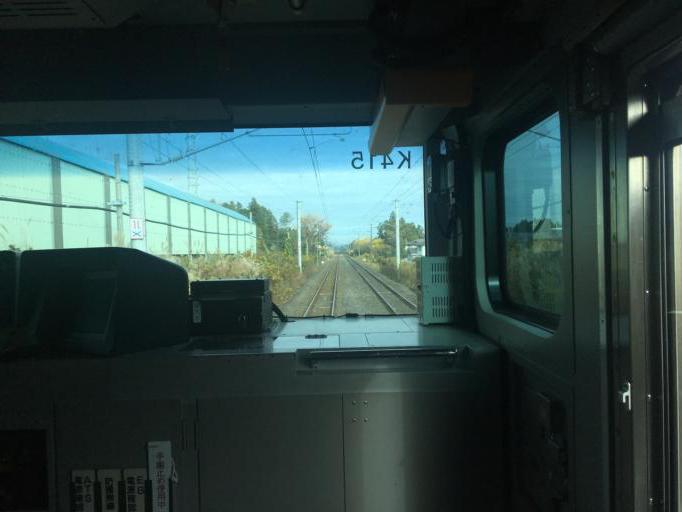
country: JP
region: Ibaraki
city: Ishioka
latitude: 36.2573
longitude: 140.2844
